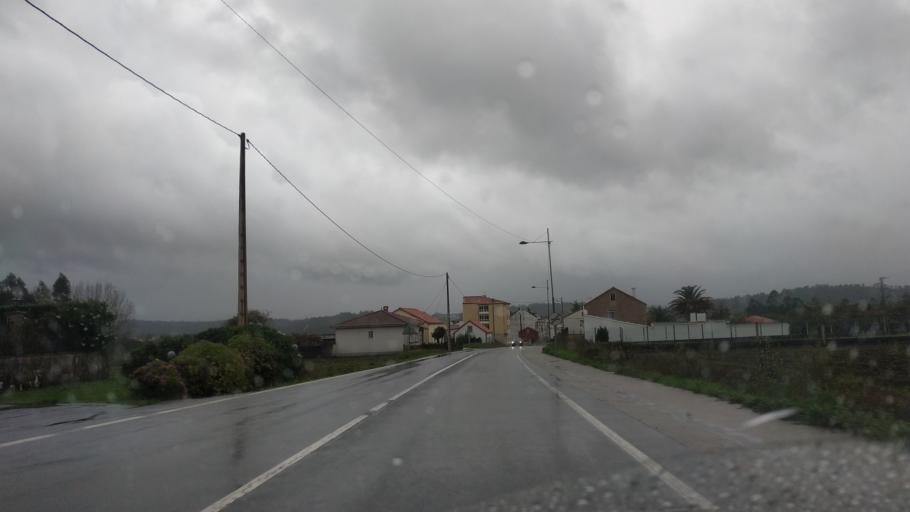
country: ES
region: Galicia
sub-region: Provincia da Coruna
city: Negreira
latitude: 42.9190
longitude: -8.7339
